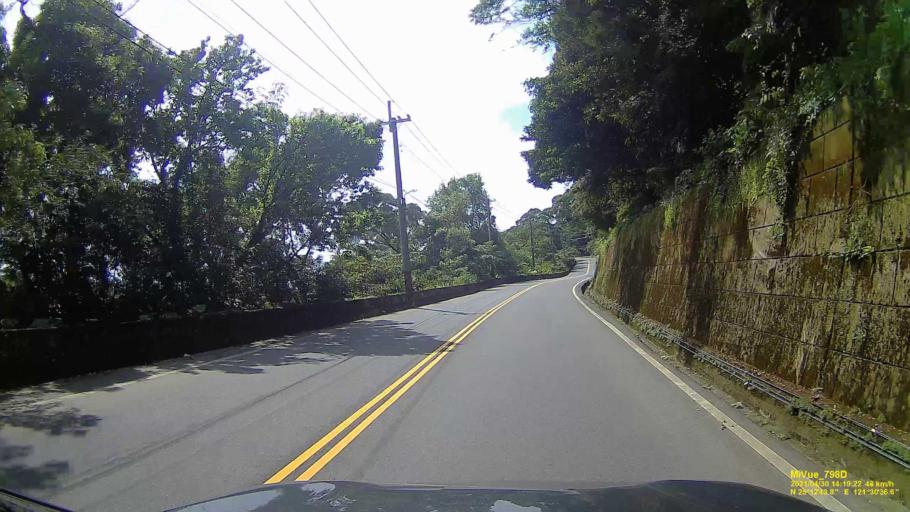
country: TW
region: Taipei
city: Taipei
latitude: 25.2124
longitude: 121.5098
